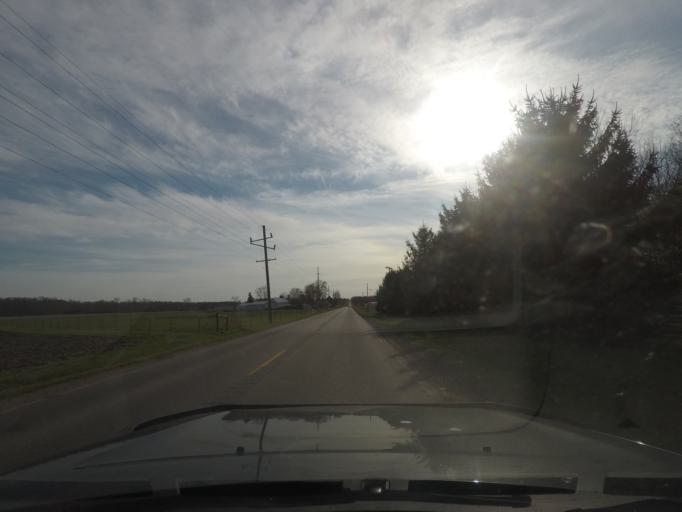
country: US
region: Indiana
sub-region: Elkhart County
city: Wakarusa
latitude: 41.5388
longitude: -85.9356
